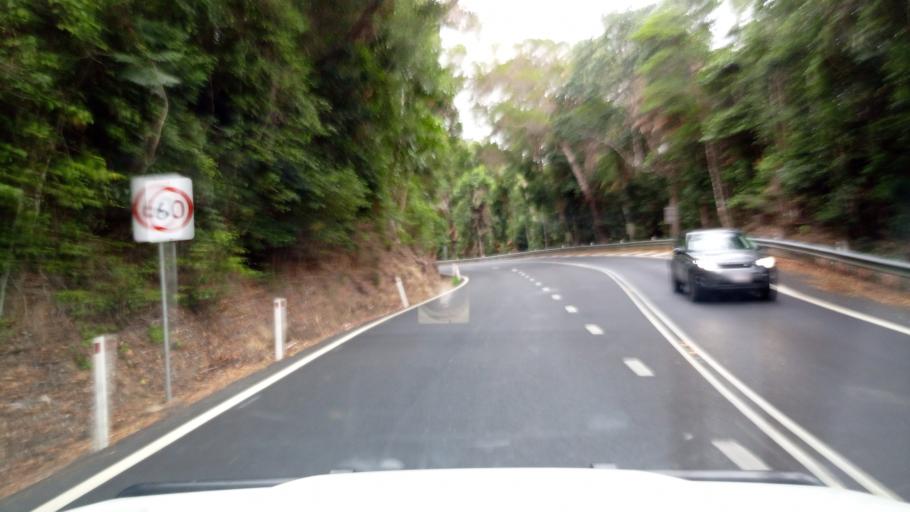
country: AU
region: Queensland
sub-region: Tablelands
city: Kuranda
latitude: -16.8317
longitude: 145.6687
